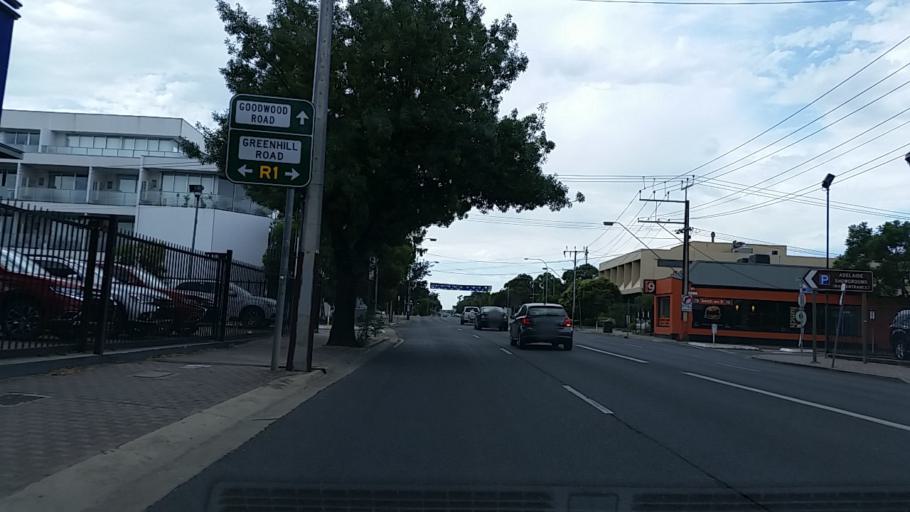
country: AU
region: South Australia
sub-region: Unley
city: Wayville
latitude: -34.9435
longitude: 138.5890
